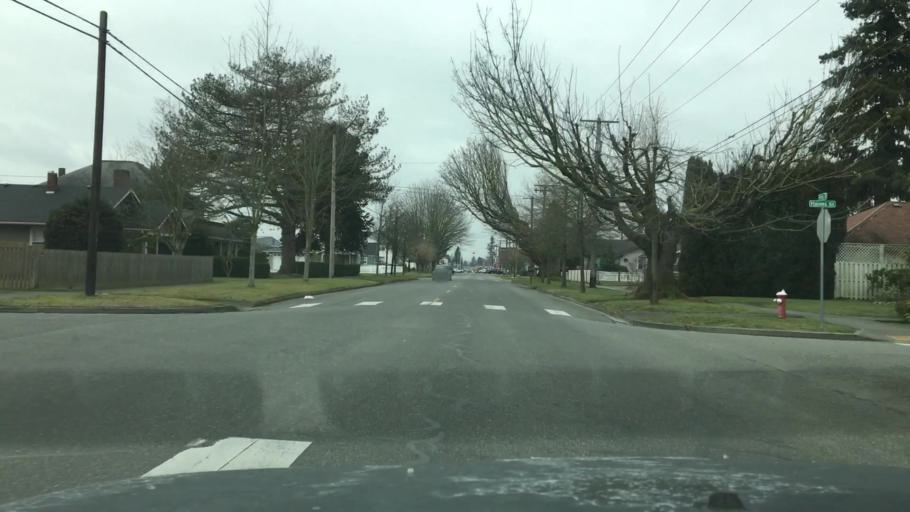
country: US
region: Washington
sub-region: Skagit County
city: Sedro-Woolley
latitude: 48.5054
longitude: -122.2325
